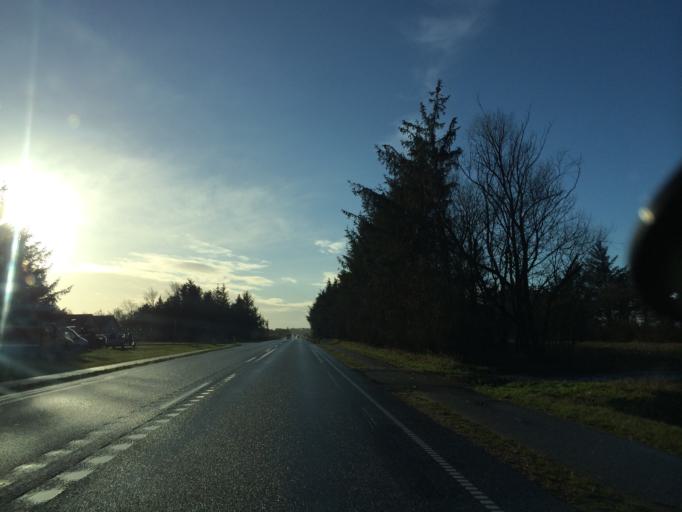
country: DK
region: Central Jutland
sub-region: Ringkobing-Skjern Kommune
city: Ringkobing
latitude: 56.1195
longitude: 8.2736
